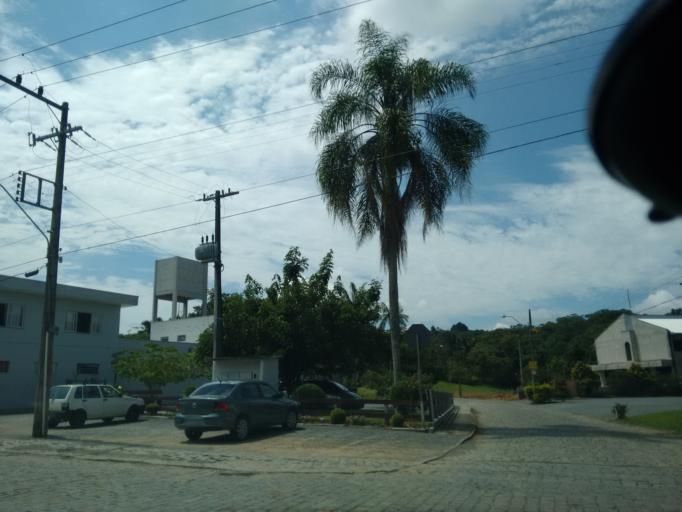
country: BR
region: Santa Catarina
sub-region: Indaial
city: Indaial
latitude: -26.8546
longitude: -49.1562
